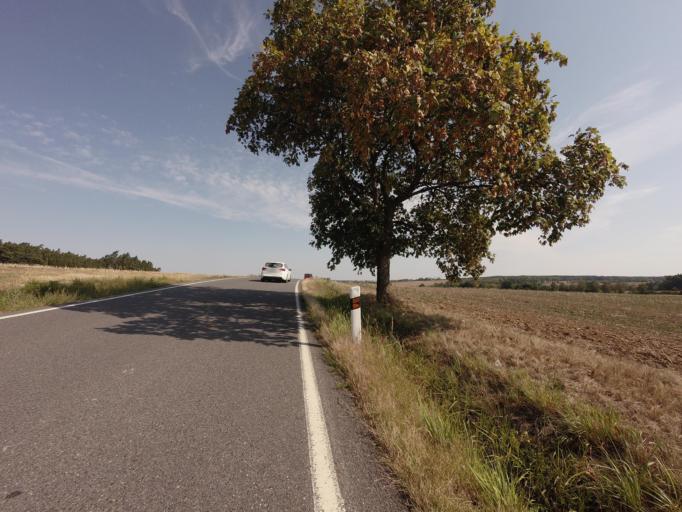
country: CZ
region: Jihocesky
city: Bernartice
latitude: 49.3508
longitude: 14.3733
